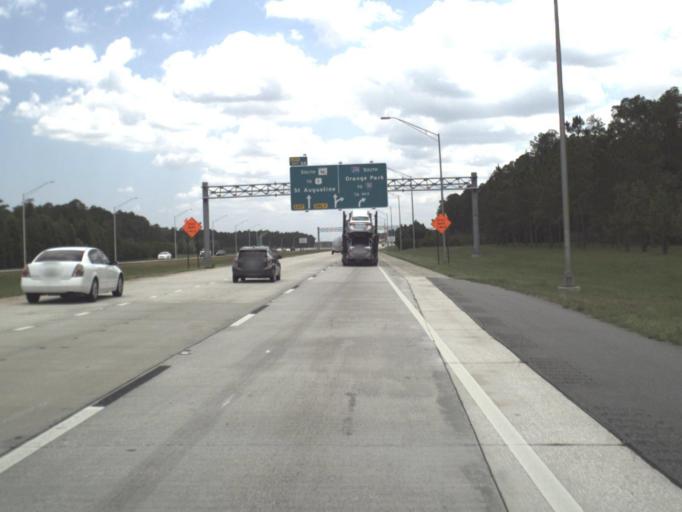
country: US
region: Florida
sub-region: Saint Johns County
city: Palm Valley
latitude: 30.1900
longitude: -81.5139
